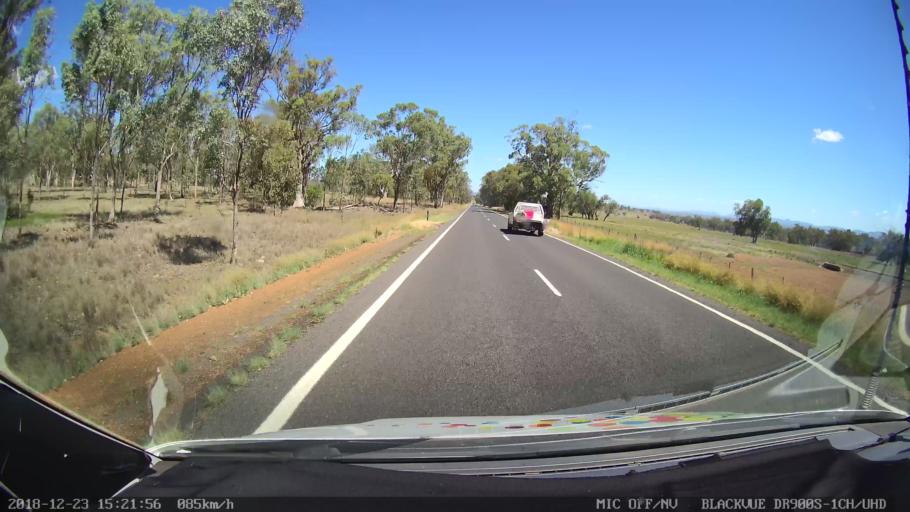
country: AU
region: New South Wales
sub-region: Tamworth Municipality
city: Manilla
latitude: -30.8625
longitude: 150.8004
